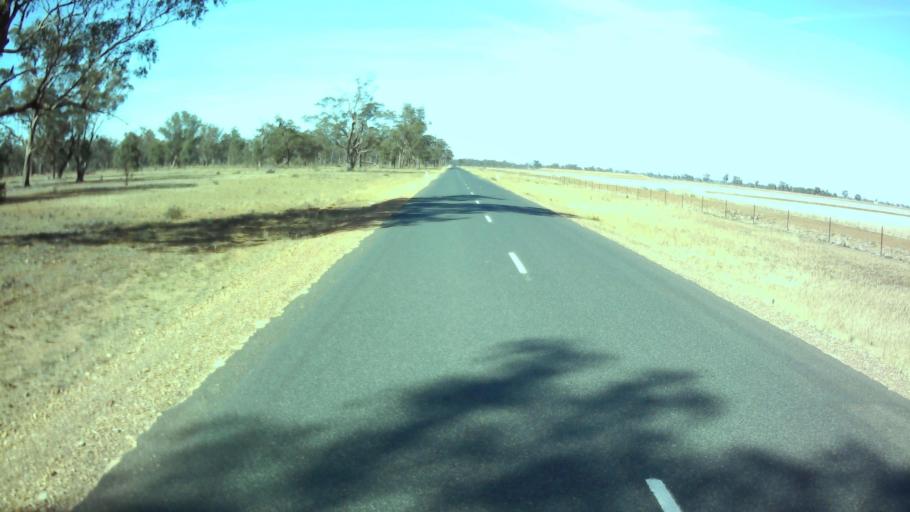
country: AU
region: New South Wales
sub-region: Weddin
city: Grenfell
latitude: -34.1210
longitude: 147.8111
